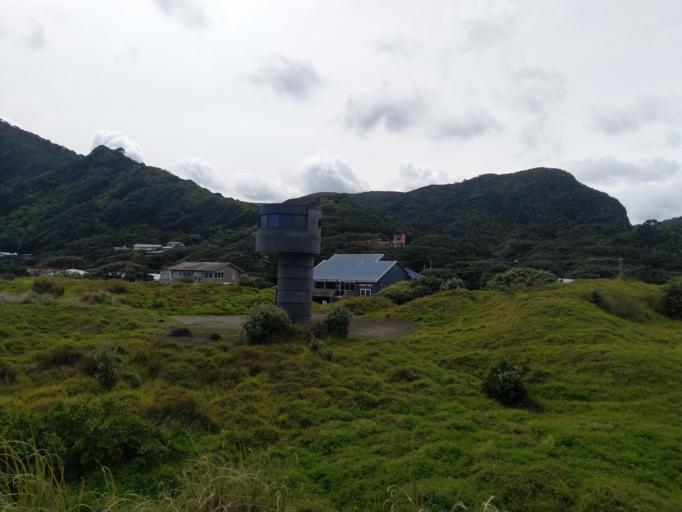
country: NZ
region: Auckland
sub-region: Auckland
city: Muriwai Beach
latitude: -36.9430
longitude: 174.4639
